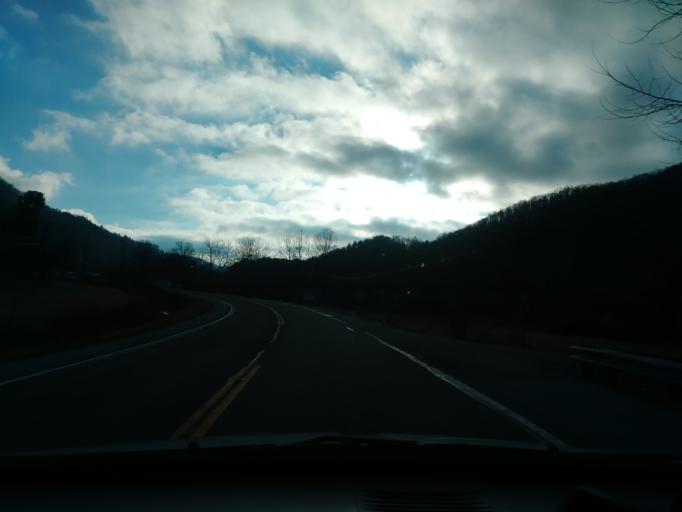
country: US
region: Tennessee
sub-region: Carter County
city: Roan Mountain
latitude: 36.2024
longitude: -82.0877
